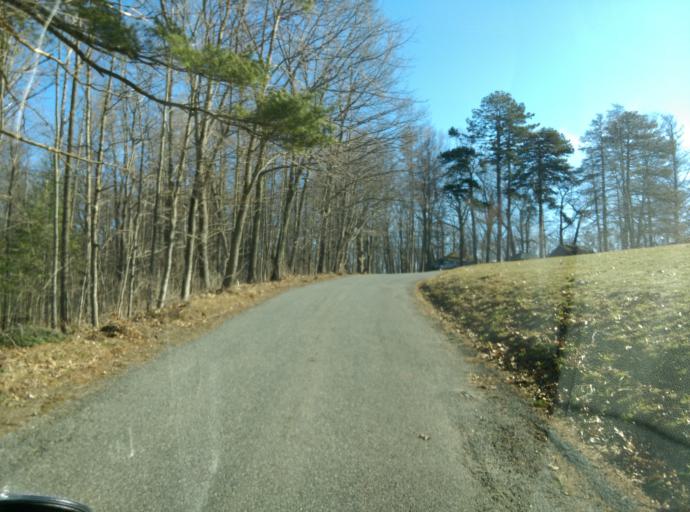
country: US
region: Massachusetts
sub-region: Essex County
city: Haverhill
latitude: 42.7891
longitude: -71.0626
